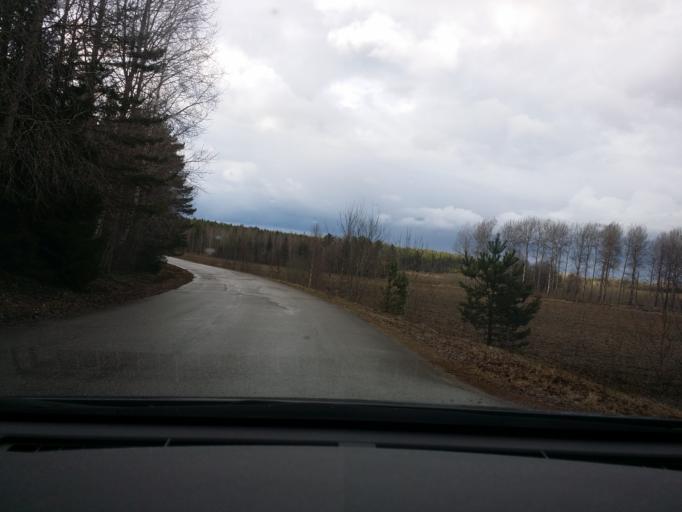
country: SE
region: Soedermanland
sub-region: Eskilstuna Kommun
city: Arla
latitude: 59.2990
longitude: 16.6865
